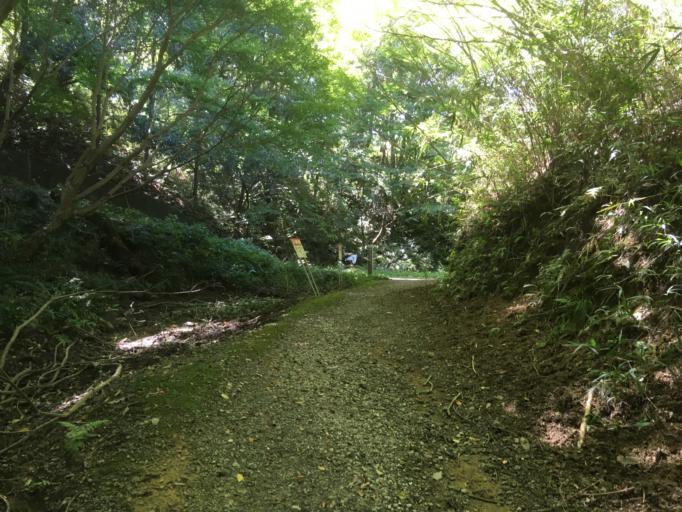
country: JP
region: Nara
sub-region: Ikoma-shi
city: Ikoma
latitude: 34.7266
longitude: 135.6739
